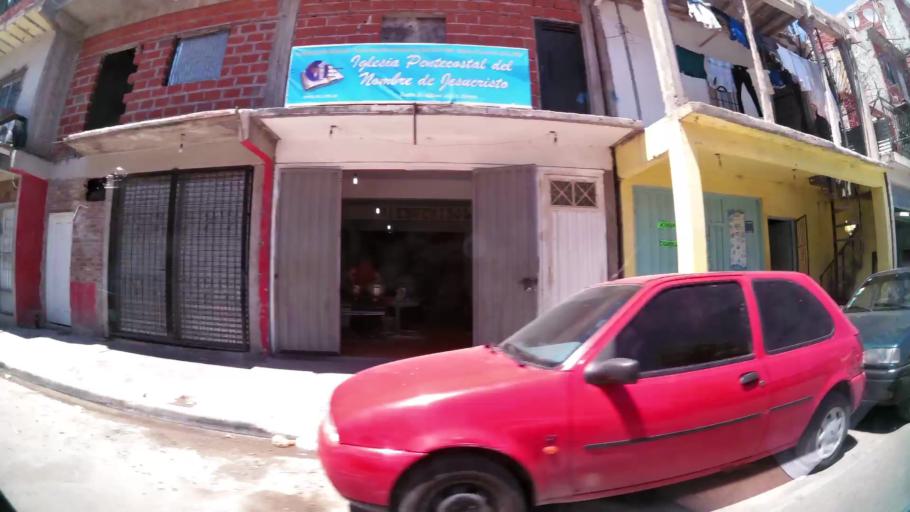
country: AR
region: Buenos Aires
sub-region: Partido de Avellaneda
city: Avellaneda
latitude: -34.6557
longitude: -58.3998
